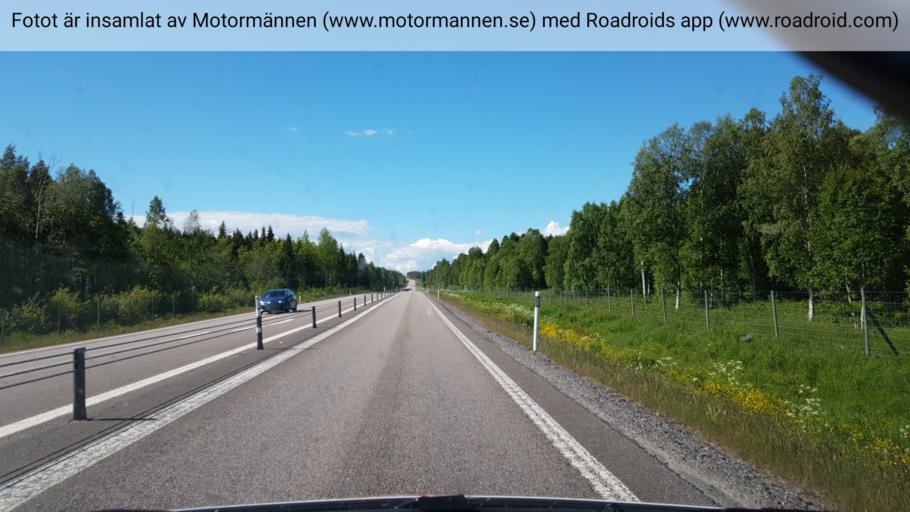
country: SE
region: Norrbotten
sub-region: Kalix Kommun
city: Rolfs
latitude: 65.8959
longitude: 22.8876
